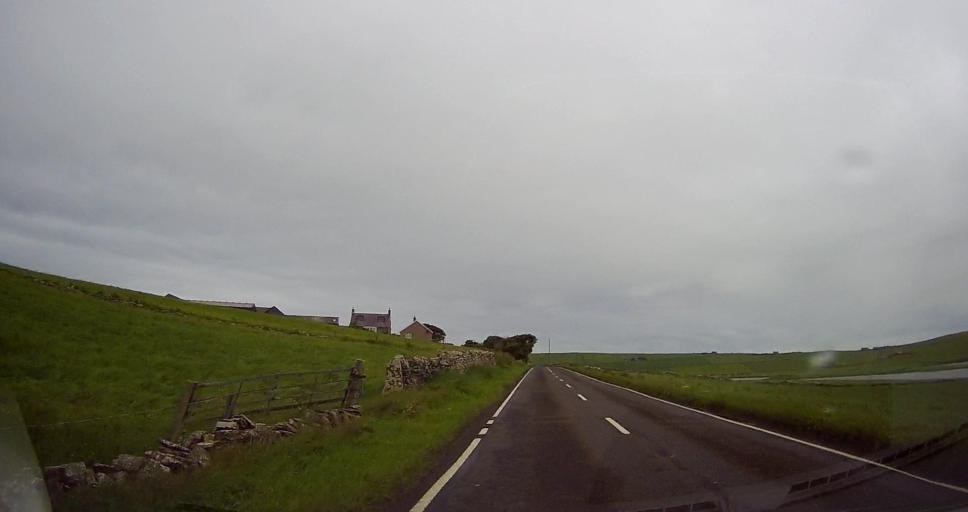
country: GB
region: Scotland
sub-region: Orkney Islands
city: Stromness
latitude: 59.0086
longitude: -3.2933
